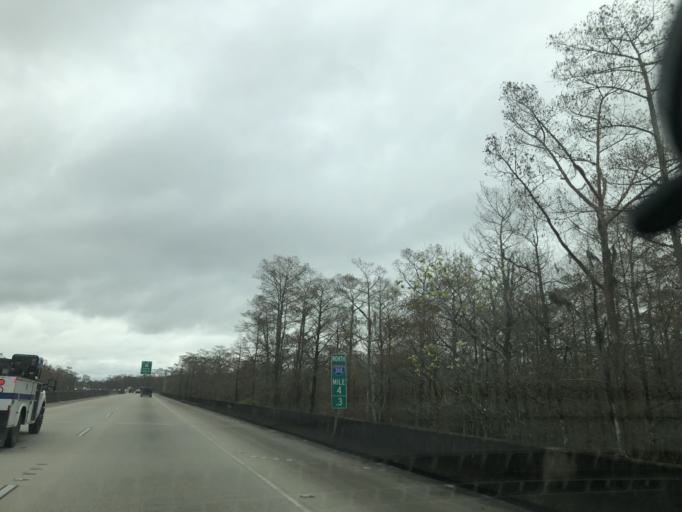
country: US
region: Louisiana
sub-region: Saint Charles Parish
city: Destrehan
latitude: 29.9652
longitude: -90.3425
